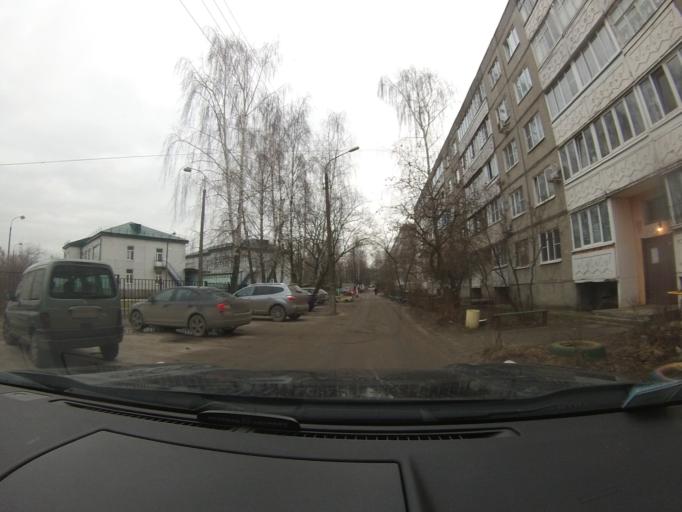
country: RU
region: Moskovskaya
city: Lopatinskiy
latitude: 55.3227
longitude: 38.7004
